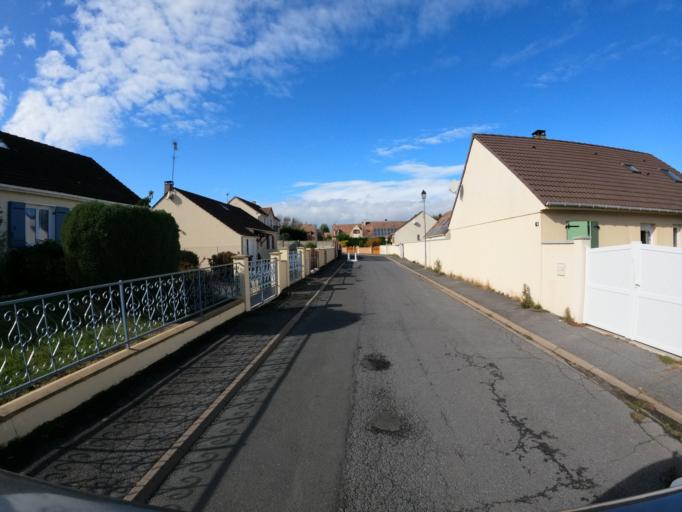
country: FR
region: Ile-de-France
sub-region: Departement de Seine-et-Marne
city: Saint-Germain-sur-Morin
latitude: 48.8791
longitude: 2.8503
